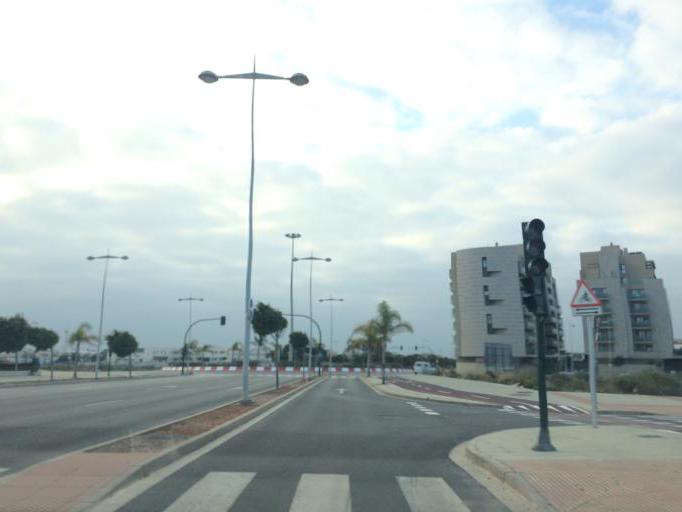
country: ES
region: Andalusia
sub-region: Provincia de Almeria
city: Almeria
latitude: 36.8290
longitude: -2.4380
